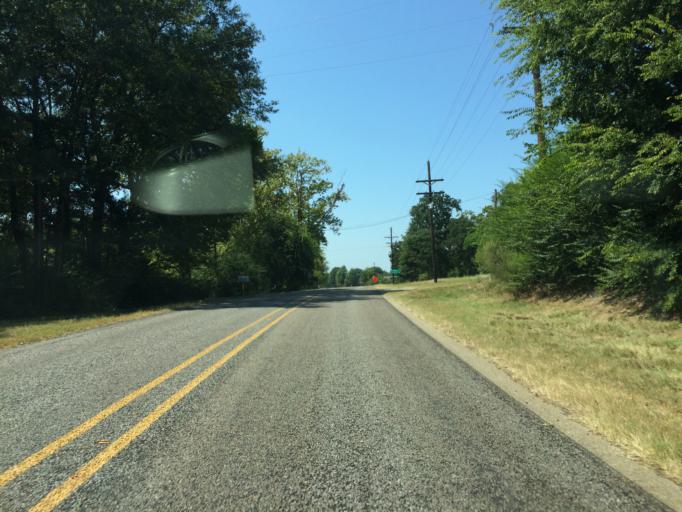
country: US
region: Texas
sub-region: Wood County
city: Quitman
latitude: 32.7413
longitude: -95.2863
